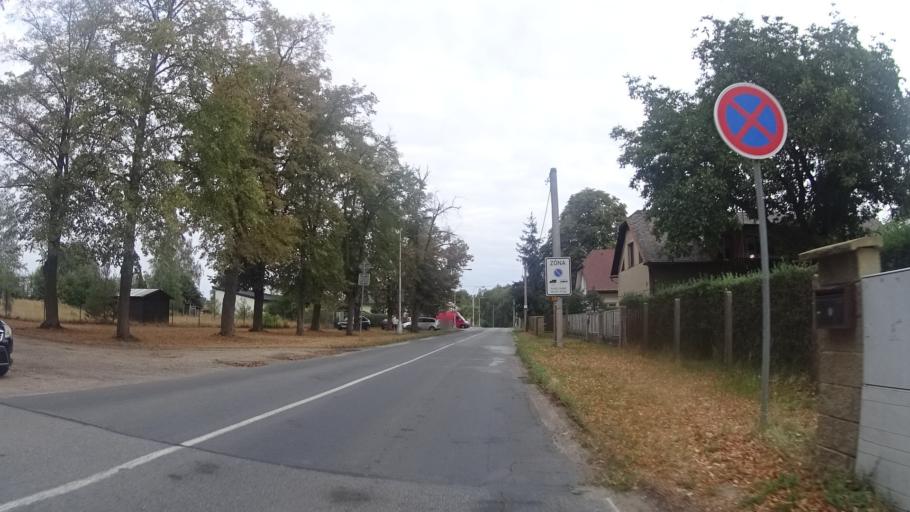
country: CZ
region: Kralovehradecky
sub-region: Okres Hradec Kralove
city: Hradec Kralove
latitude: 50.2060
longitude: 15.8888
